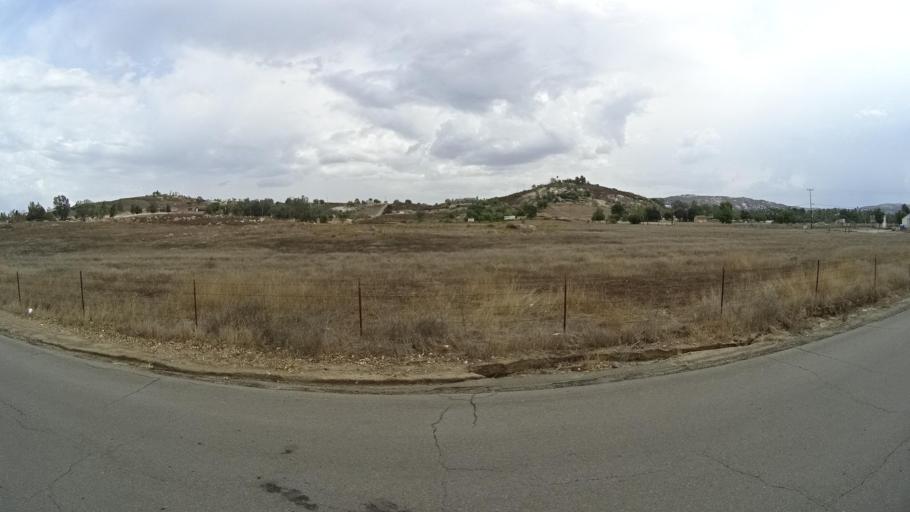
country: US
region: California
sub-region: San Diego County
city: Ramona
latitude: 33.0740
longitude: -116.8592
